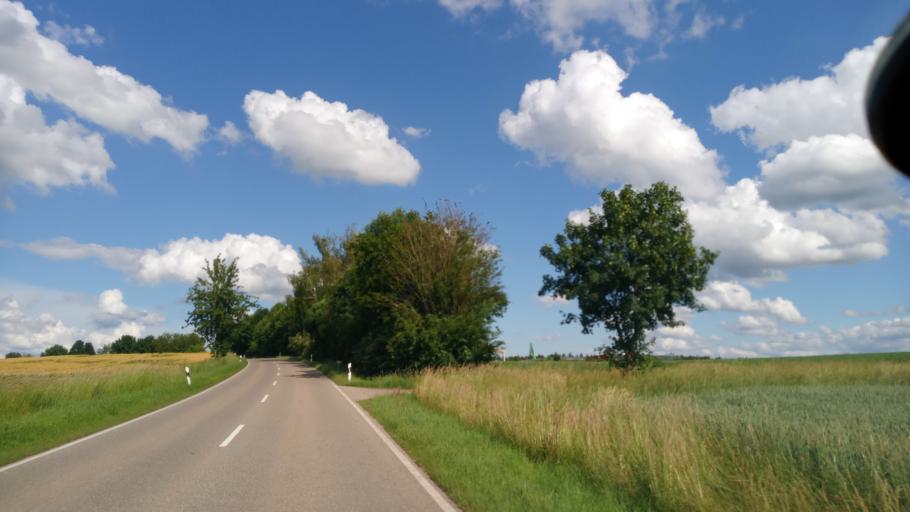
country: DE
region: Bavaria
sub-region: Upper Bavaria
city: Rohrmoos
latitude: 48.3560
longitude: 11.4321
